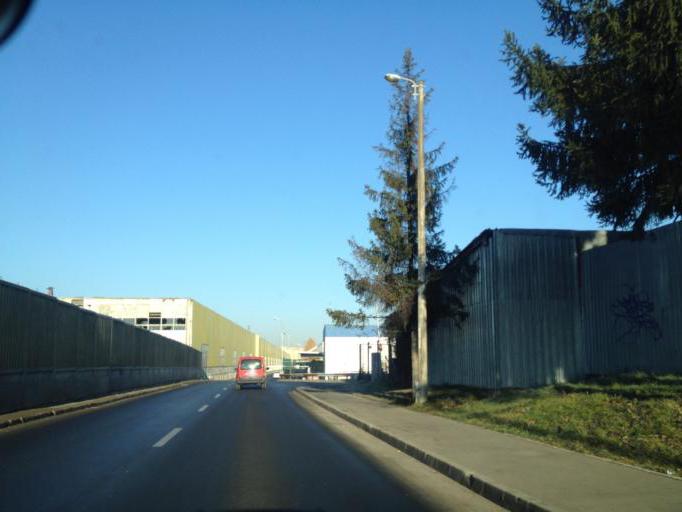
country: RO
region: Brasov
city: Brasov
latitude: 45.6288
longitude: 25.6379
